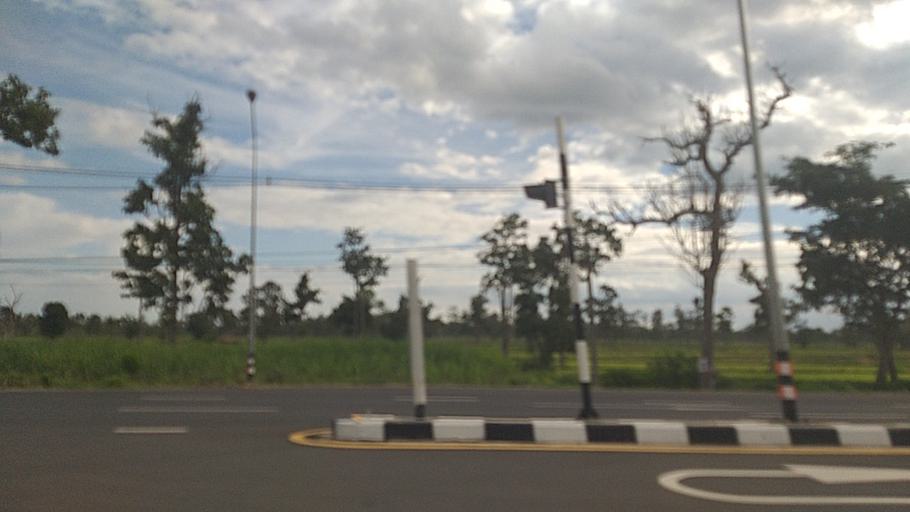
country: TH
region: Surin
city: Kap Choeng
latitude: 14.5385
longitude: 103.5226
